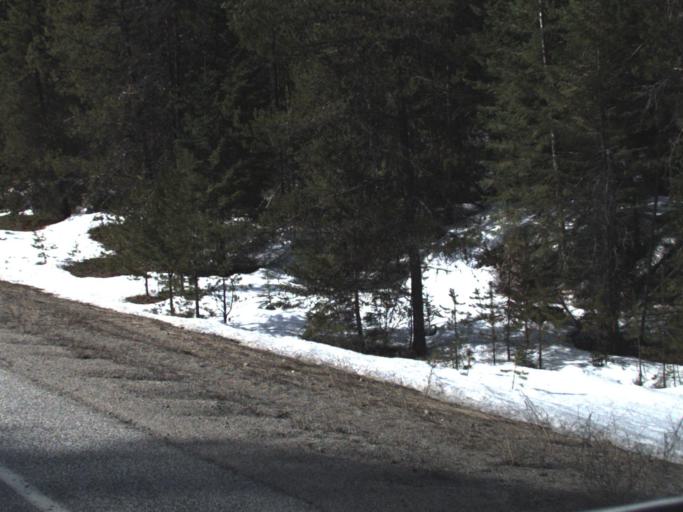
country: US
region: Washington
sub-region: Stevens County
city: Chewelah
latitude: 48.5622
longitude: -117.5554
